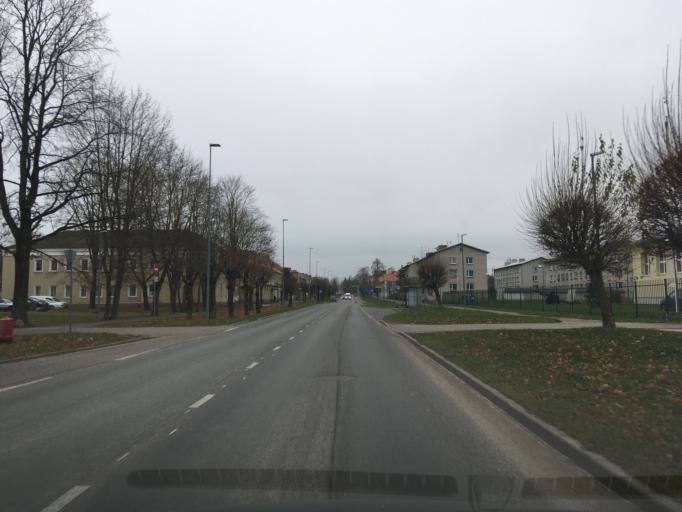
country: EE
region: Ida-Virumaa
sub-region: Johvi vald
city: Johvi
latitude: 59.3632
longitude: 27.4113
